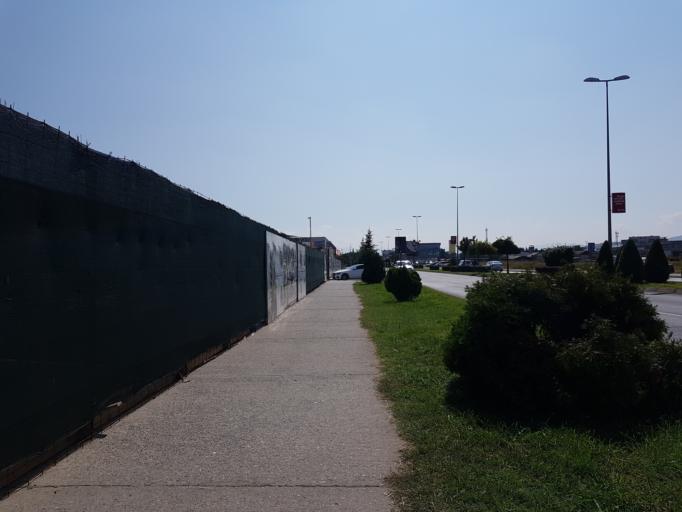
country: ME
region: Podgorica
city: Podgorica
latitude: 42.4307
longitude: 19.2728
